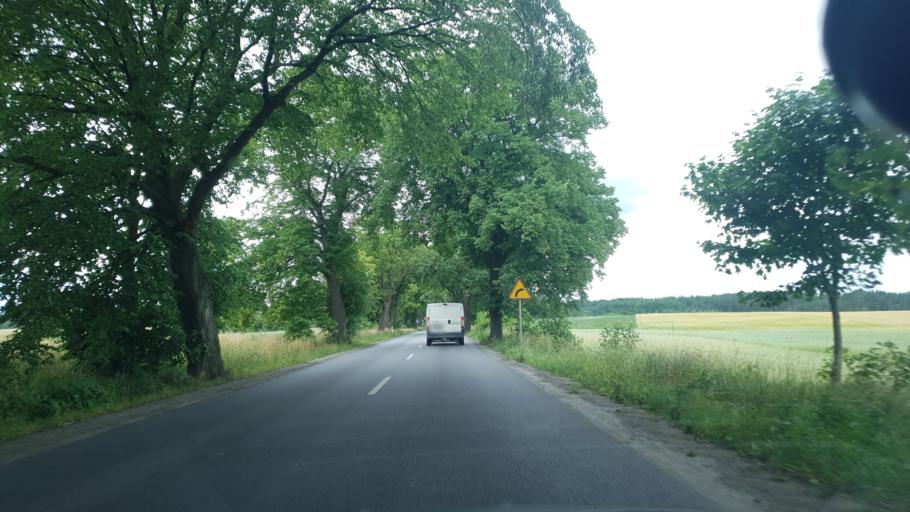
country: PL
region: Pomeranian Voivodeship
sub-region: Powiat kartuski
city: Zukowo
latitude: 54.3824
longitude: 18.3508
